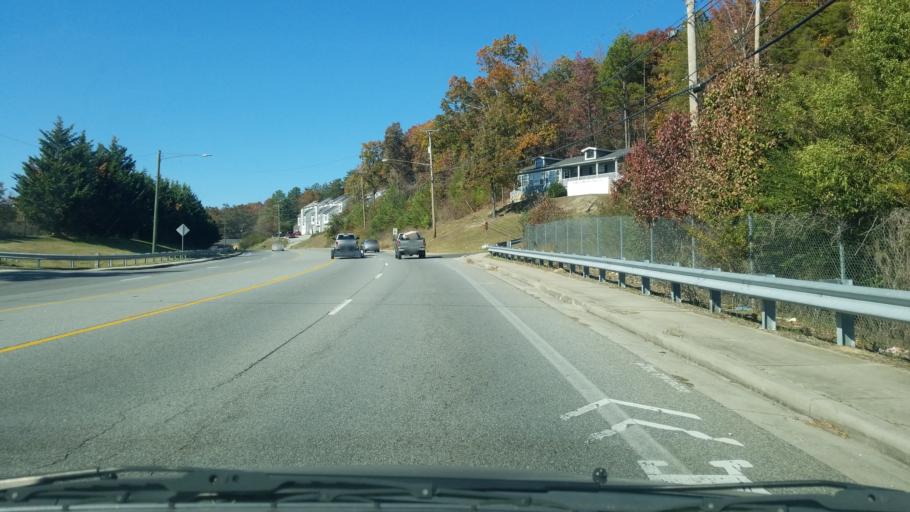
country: US
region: Tennessee
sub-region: Hamilton County
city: Red Bank
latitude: 35.1160
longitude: -85.2625
